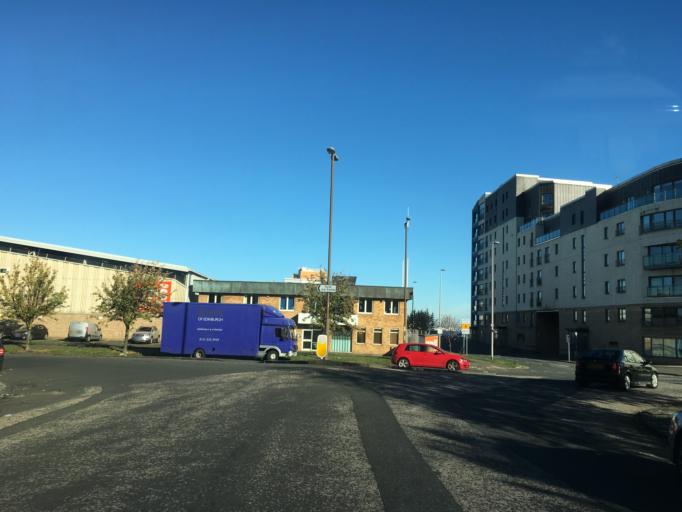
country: GB
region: Scotland
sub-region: Edinburgh
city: Edinburgh
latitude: 55.9809
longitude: -3.2247
